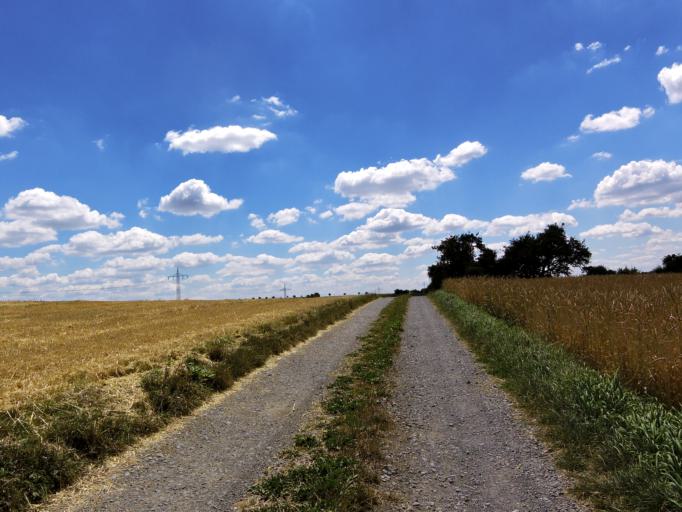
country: DE
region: Bavaria
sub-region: Regierungsbezirk Unterfranken
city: Gadheim
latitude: 49.8295
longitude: 9.9287
